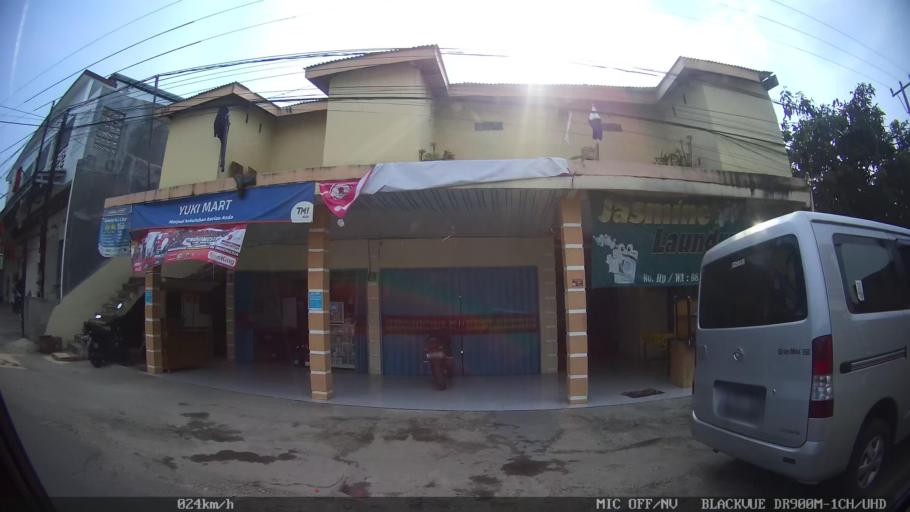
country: ID
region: Lampung
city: Kedaton
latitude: -5.3670
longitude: 105.2209
